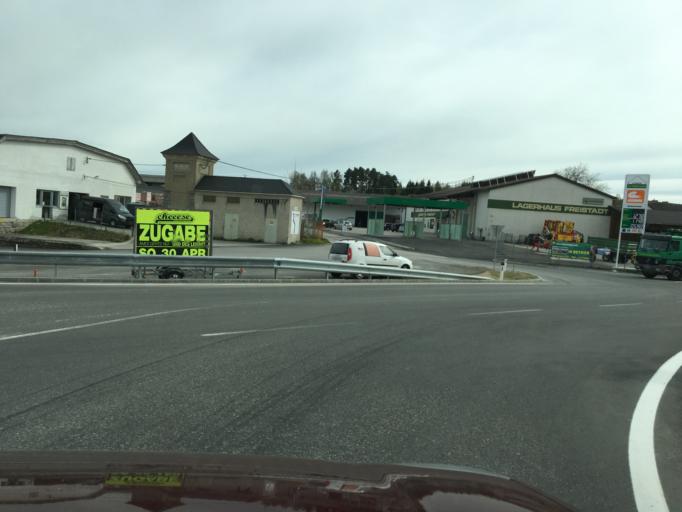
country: AT
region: Upper Austria
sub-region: Politischer Bezirk Freistadt
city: Freistadt
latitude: 48.4967
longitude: 14.4865
